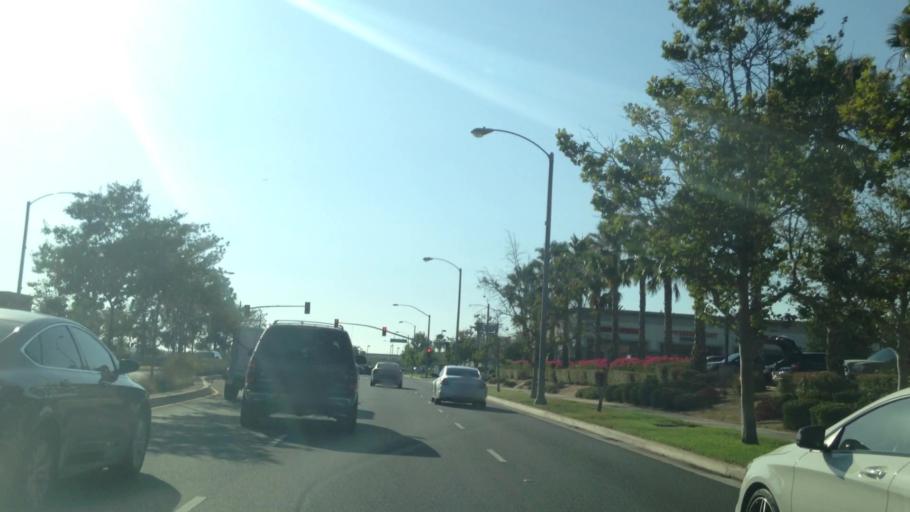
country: US
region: California
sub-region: Riverside County
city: Moreno Valley
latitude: 33.9403
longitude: -117.2810
